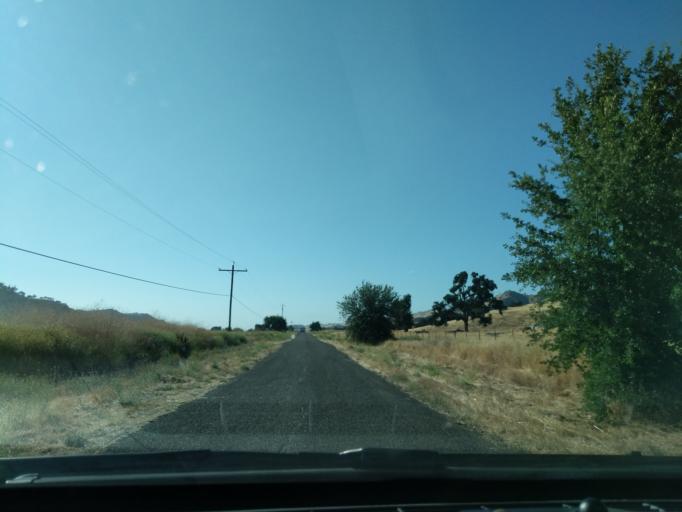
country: US
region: California
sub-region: Monterey County
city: King City
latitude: 36.1441
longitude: -120.7541
